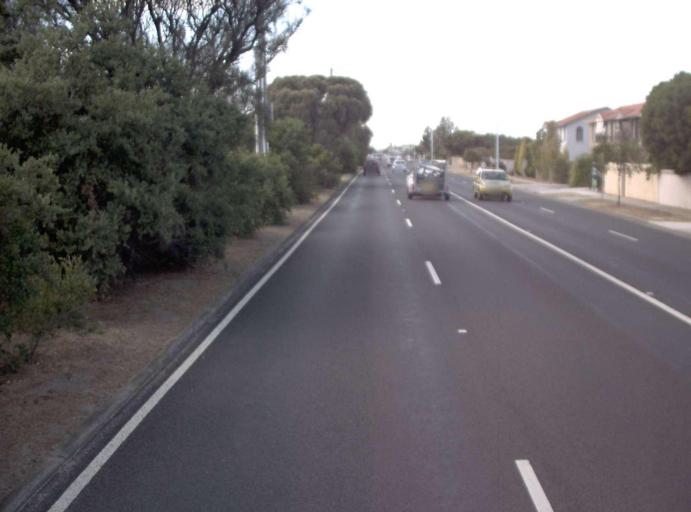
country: AU
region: Victoria
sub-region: Kingston
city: Aspendale
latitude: -38.0316
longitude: 145.1044
